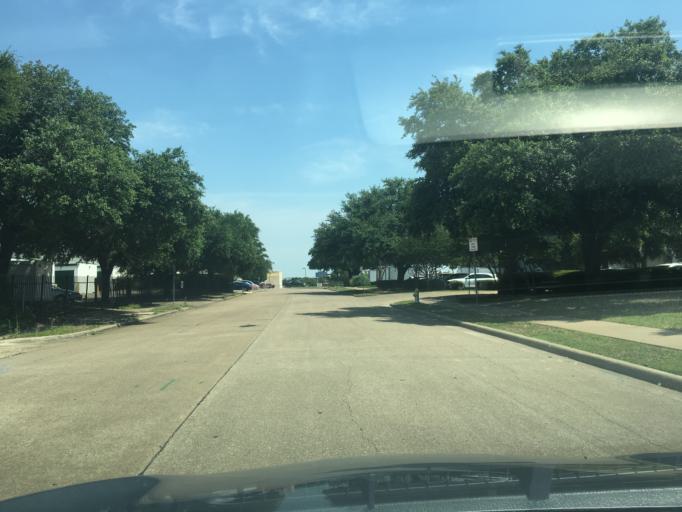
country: US
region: Texas
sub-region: Dallas County
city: Richardson
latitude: 32.9557
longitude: -96.7120
